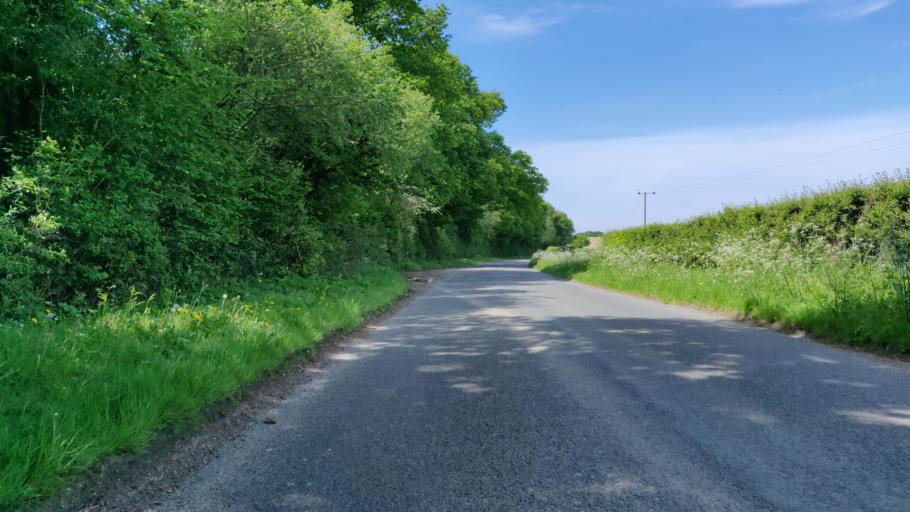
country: GB
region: England
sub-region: West Sussex
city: Southwater
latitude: 51.0472
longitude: -0.3732
